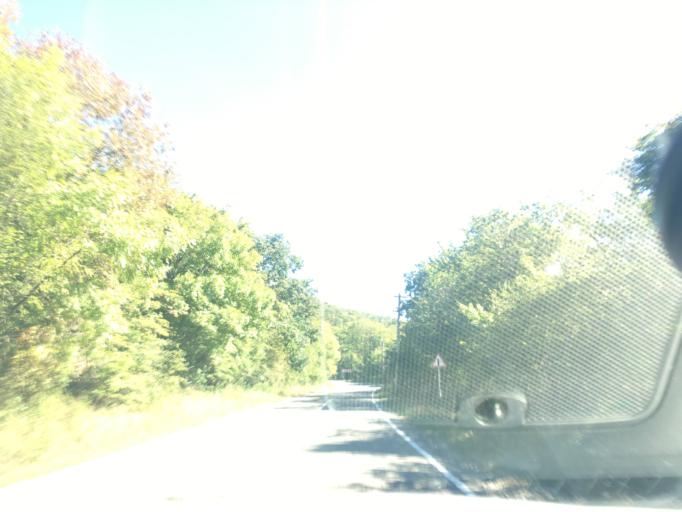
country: GE
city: Didi Lilo
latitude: 41.8868
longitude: 44.9209
